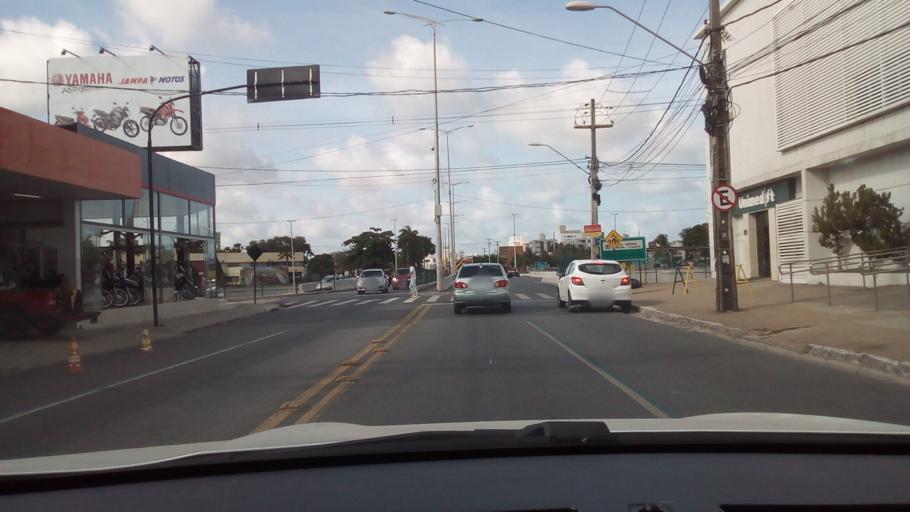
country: BR
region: Paraiba
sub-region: Joao Pessoa
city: Joao Pessoa
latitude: -7.1626
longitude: -34.8384
